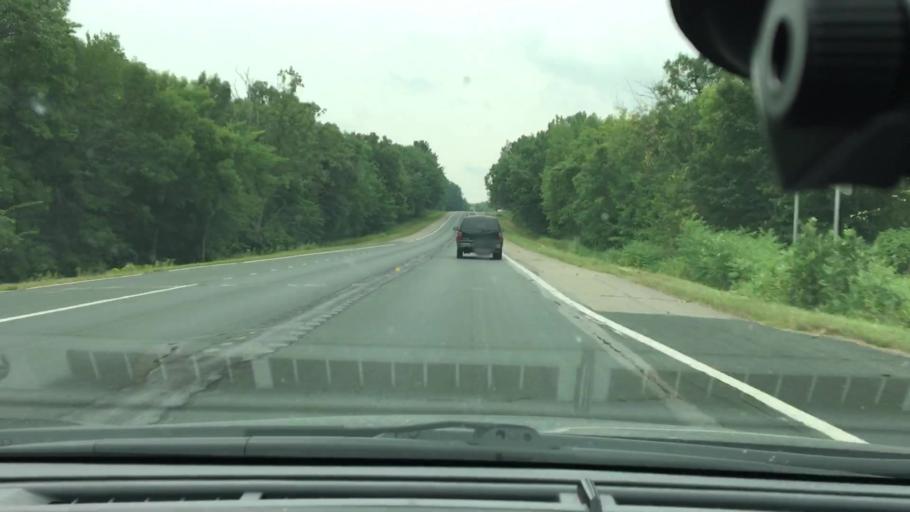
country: US
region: Minnesota
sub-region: Mille Lacs County
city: Vineland
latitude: 46.2290
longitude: -93.7935
